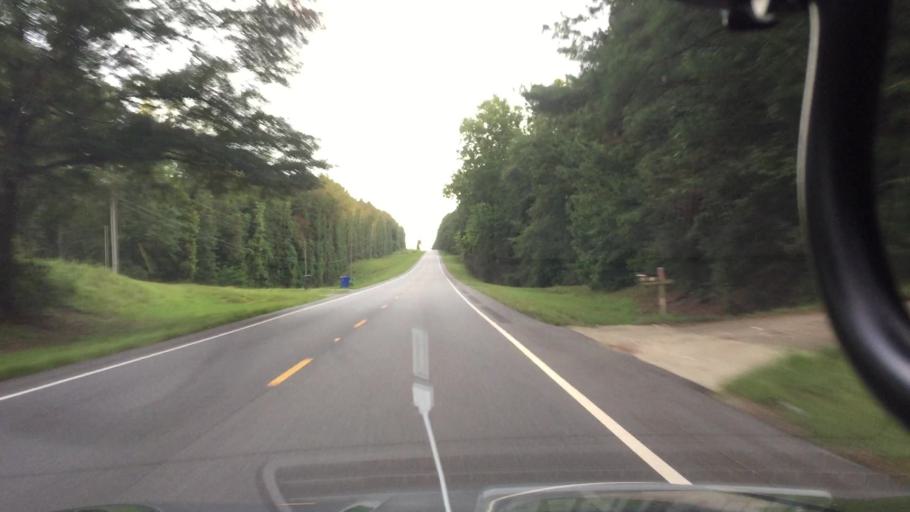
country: US
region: Alabama
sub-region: Coffee County
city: New Brockton
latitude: 31.5256
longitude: -85.9176
